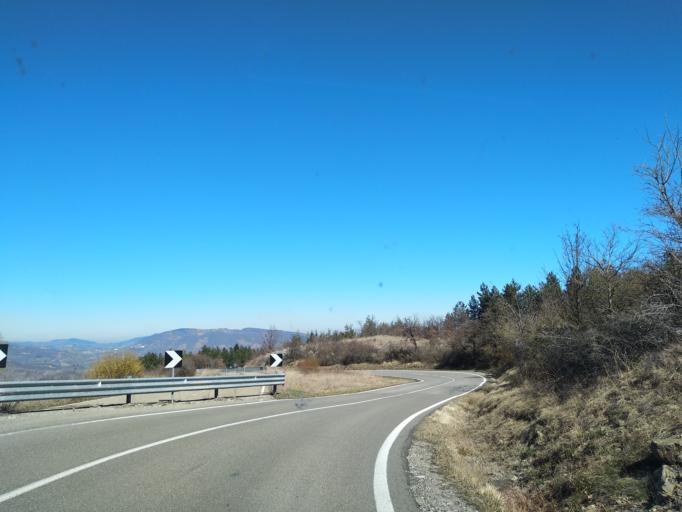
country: IT
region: Emilia-Romagna
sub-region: Provincia di Reggio Emilia
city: Busana
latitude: 44.4075
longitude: 10.3258
